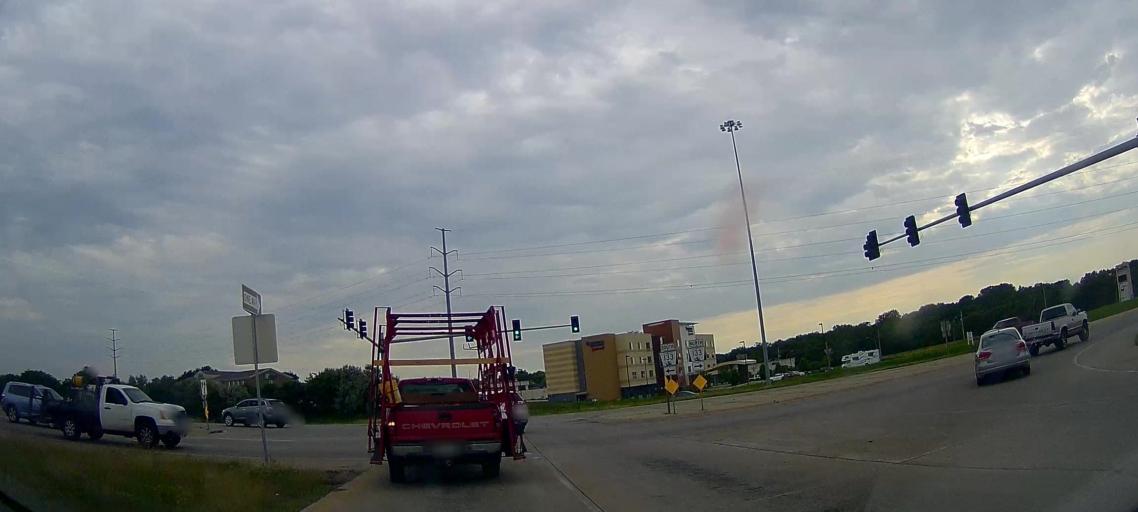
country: US
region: Nebraska
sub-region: Douglas County
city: Bennington
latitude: 41.3234
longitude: -96.0700
